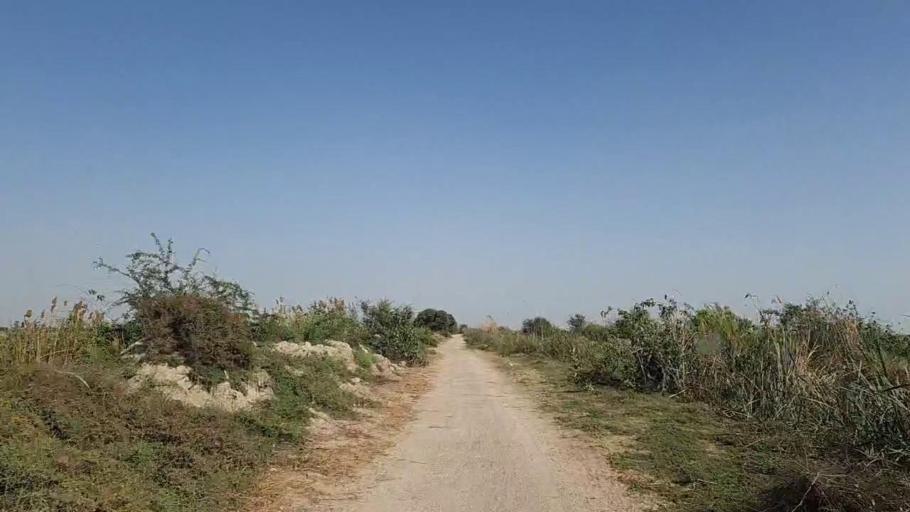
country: PK
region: Sindh
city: Chuhar Jamali
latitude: 24.4826
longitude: 68.1002
